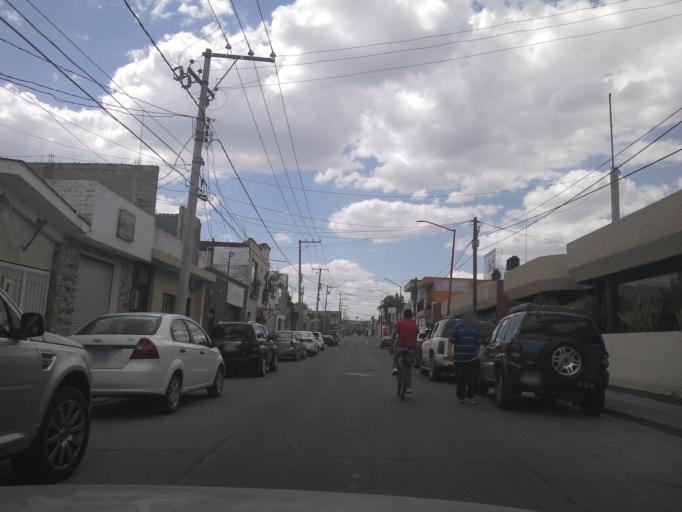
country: MX
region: Guanajuato
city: San Francisco del Rincon
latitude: 21.0273
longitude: -101.8600
